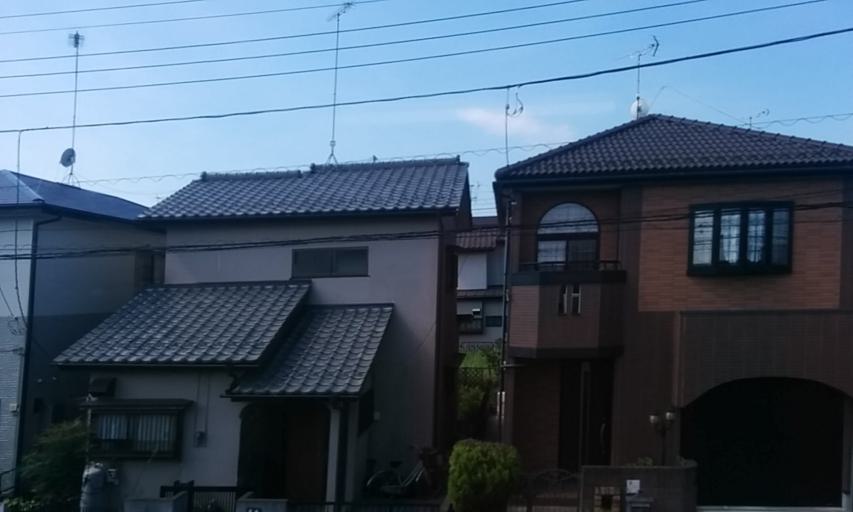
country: JP
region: Saitama
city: Kazo
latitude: 36.1130
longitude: 139.6242
